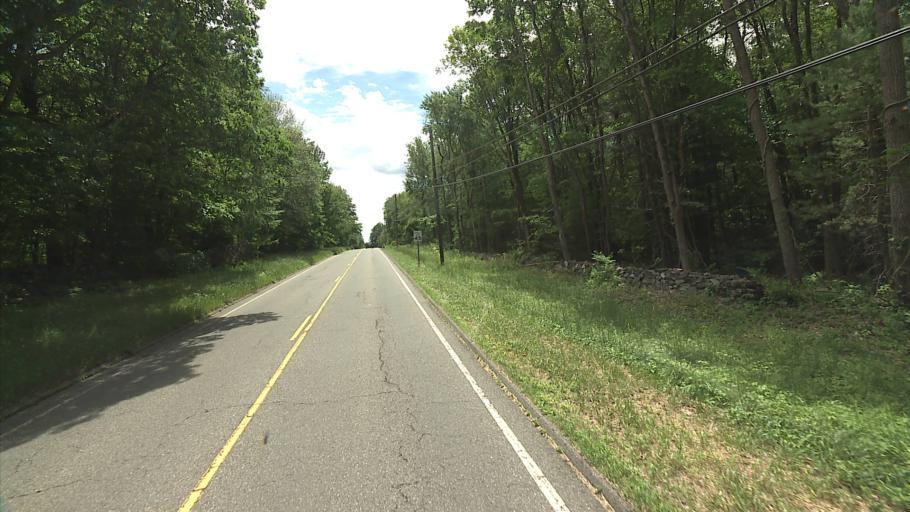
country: US
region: Connecticut
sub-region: Litchfield County
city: Litchfield
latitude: 41.7057
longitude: -73.1844
